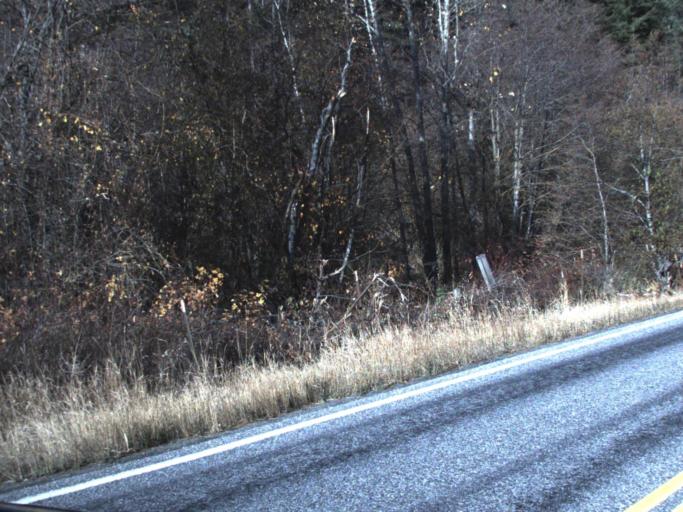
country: US
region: Washington
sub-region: Ferry County
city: Republic
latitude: 48.7926
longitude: -118.6165
